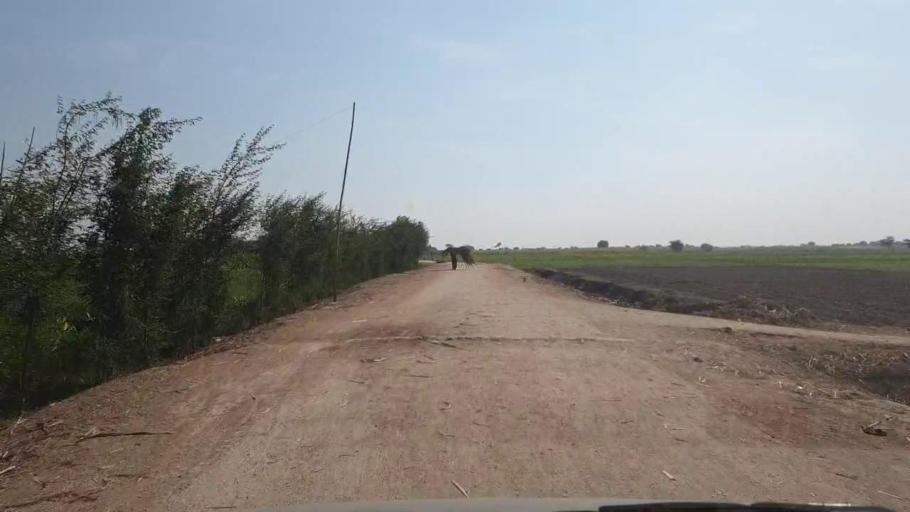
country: PK
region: Sindh
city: Chambar
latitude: 25.3490
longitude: 68.8302
